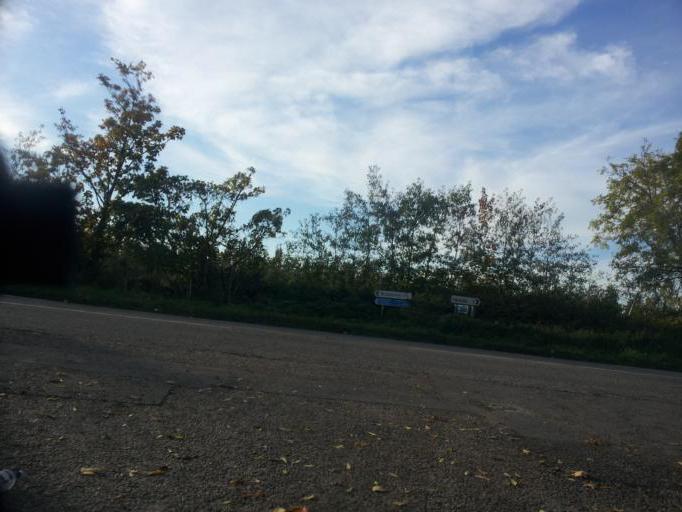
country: GB
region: England
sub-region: Kent
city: Sittingbourne
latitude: 51.3635
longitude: 0.7255
